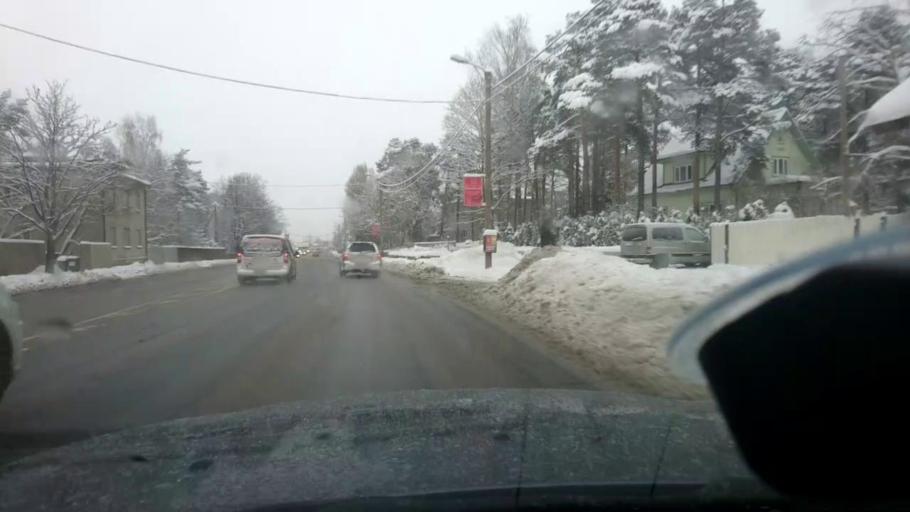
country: EE
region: Harju
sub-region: Tallinna linn
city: Tallinn
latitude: 59.3892
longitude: 24.7205
